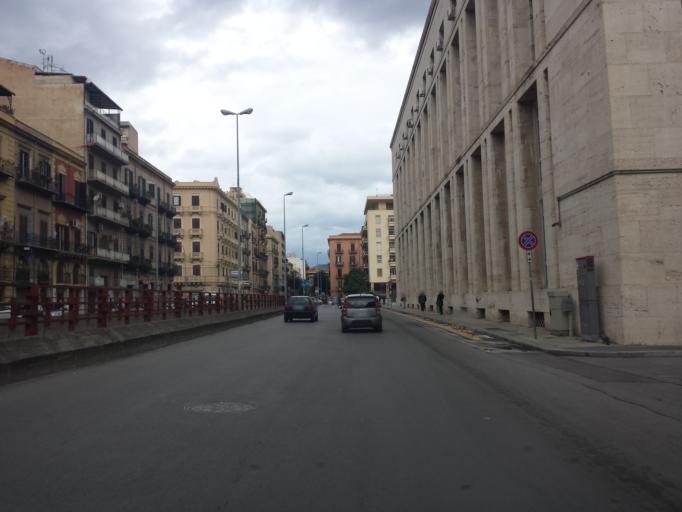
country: IT
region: Sicily
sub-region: Palermo
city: Palermo
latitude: 38.1180
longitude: 13.3511
